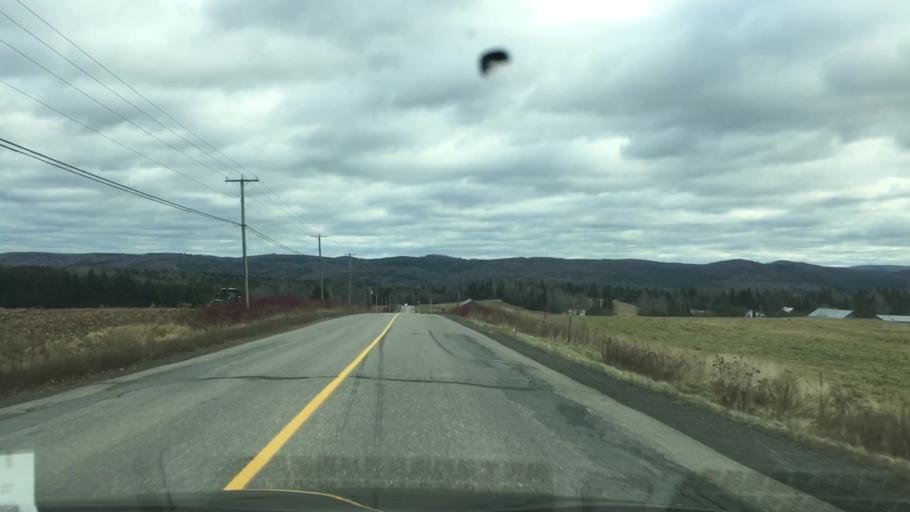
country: US
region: Maine
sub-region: Aroostook County
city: Fort Fairfield
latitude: 46.7486
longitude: -67.7415
